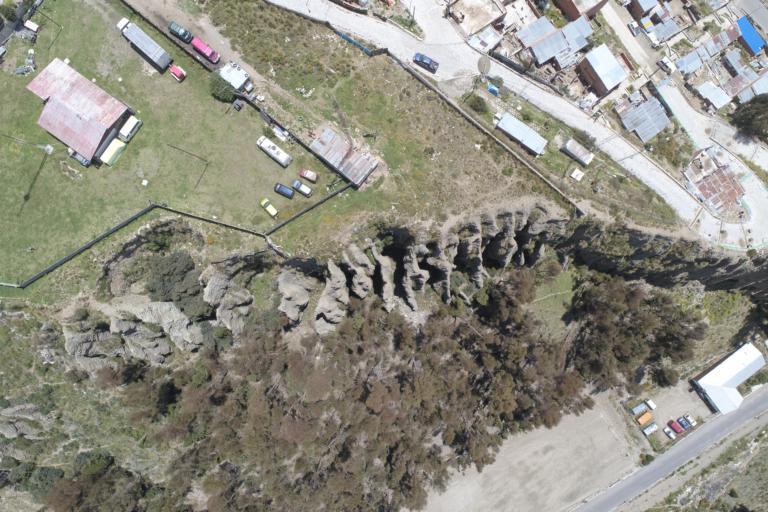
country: BO
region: La Paz
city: La Paz
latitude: -16.5289
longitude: -68.1445
